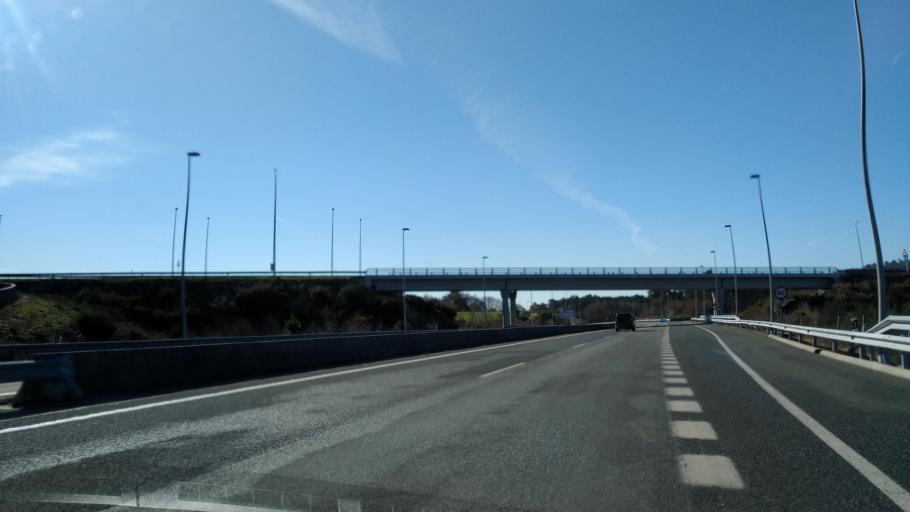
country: ES
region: Galicia
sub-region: Provincia de Ourense
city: Pinor
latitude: 42.5248
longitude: -8.0175
